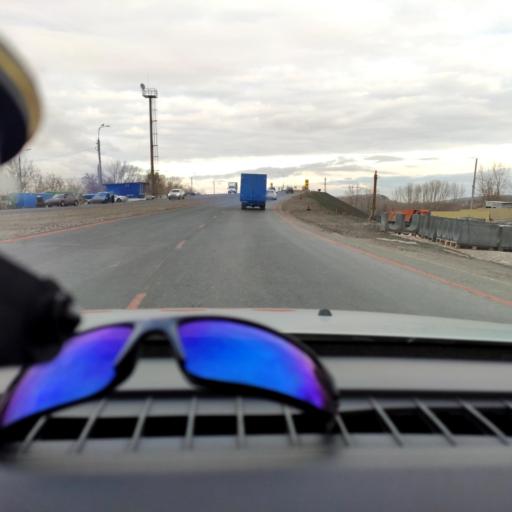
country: RU
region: Samara
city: Volzhskiy
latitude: 53.4096
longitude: 50.1414
